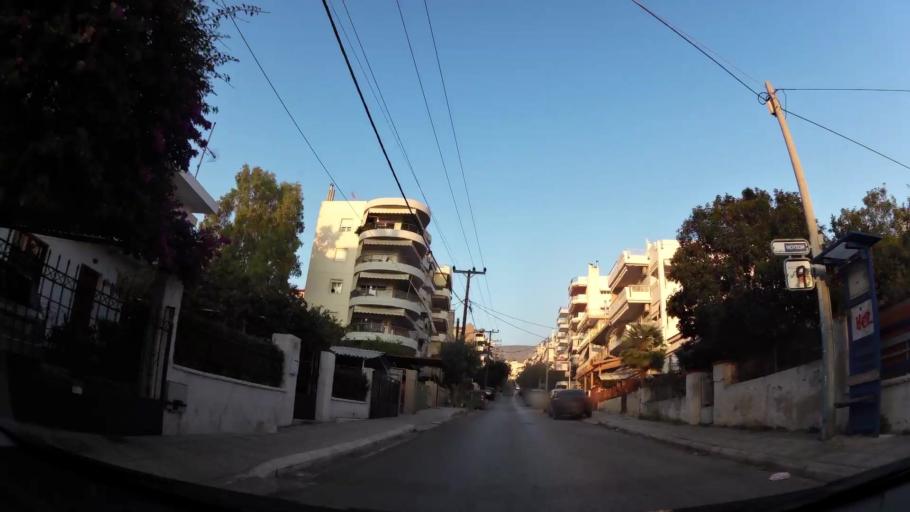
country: GR
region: Attica
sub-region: Nomarchia Athinas
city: Glyfada
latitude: 37.8845
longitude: 23.7701
